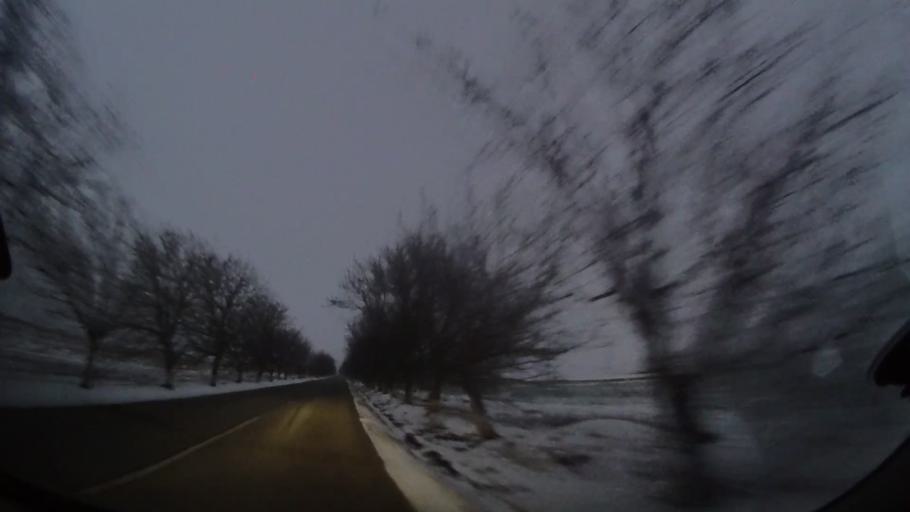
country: RO
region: Vaslui
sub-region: Comuna Dimitrie Cantemir
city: Dimitrie Cantemir
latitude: 46.5146
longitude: 28.0312
